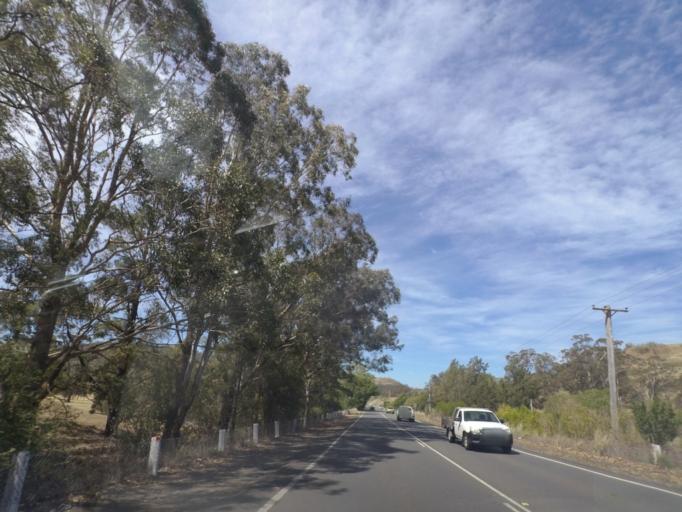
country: AU
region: New South Wales
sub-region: Wollondilly
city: Picton
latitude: -34.1669
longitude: 150.6288
